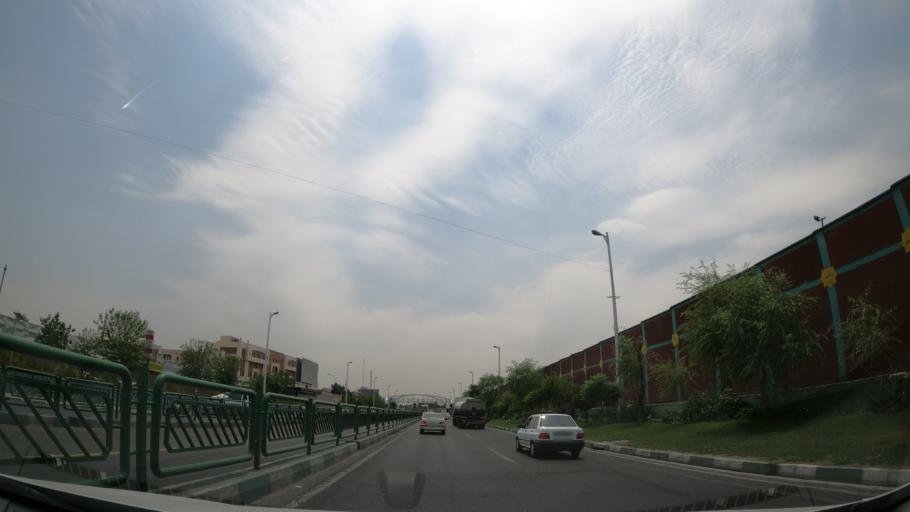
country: IR
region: Tehran
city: Tehran
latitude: 35.6924
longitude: 51.3408
